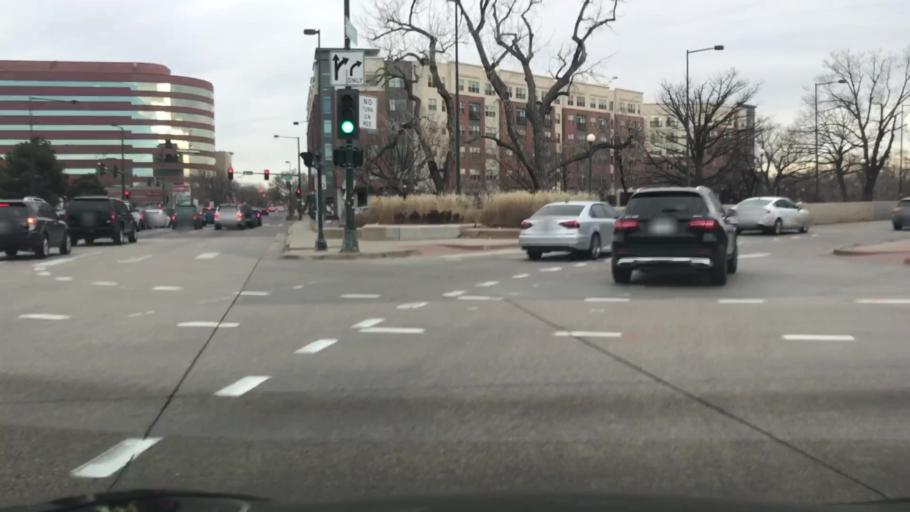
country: US
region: Colorado
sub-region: Denver County
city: Denver
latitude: 39.7256
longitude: -104.9863
